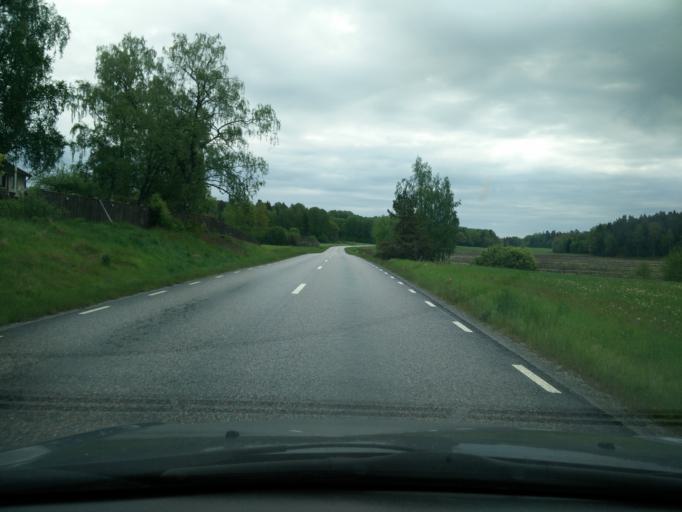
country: SE
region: Stockholm
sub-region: Norrtalje Kommun
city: Norrtalje
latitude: 59.7832
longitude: 18.7852
